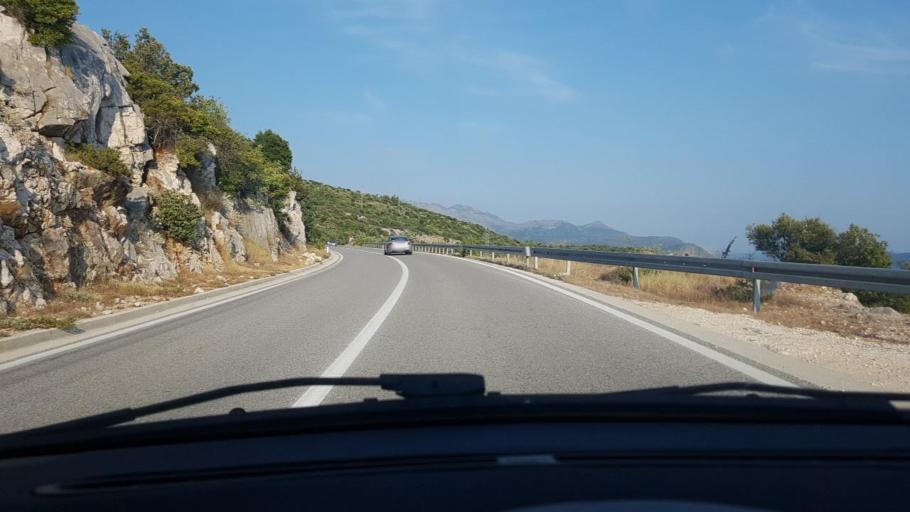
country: HR
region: Dubrovacko-Neretvanska
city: Podgora
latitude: 42.8106
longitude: 17.8051
